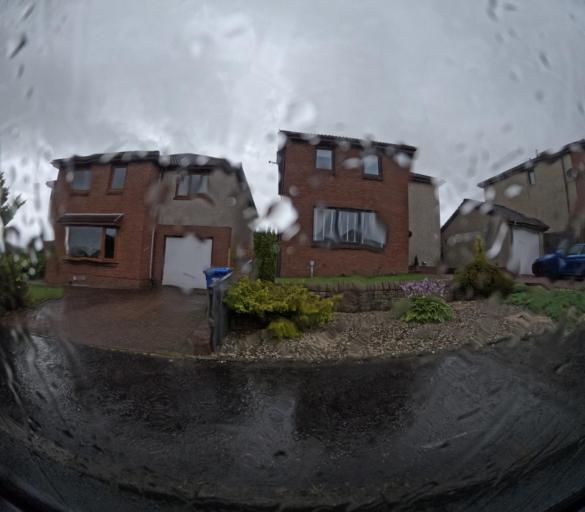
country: GB
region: Scotland
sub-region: West Lothian
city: West Calder
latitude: 55.8756
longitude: -3.5913
